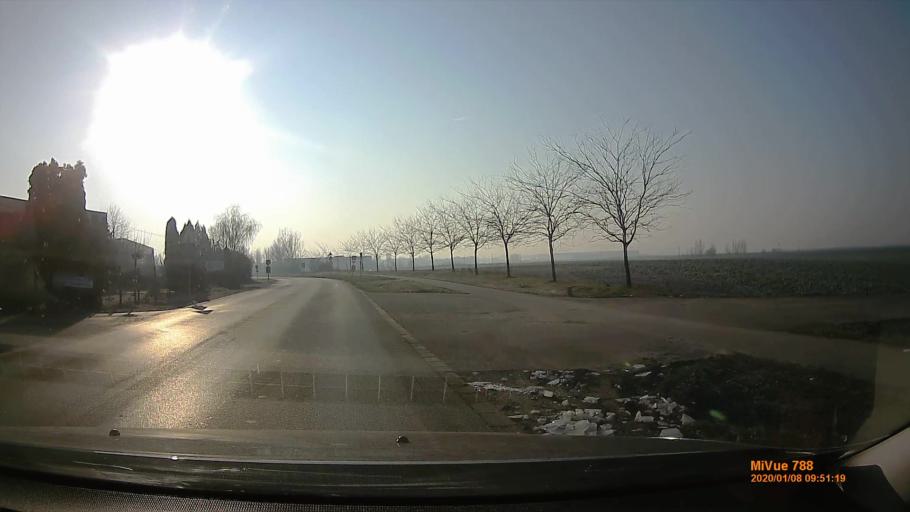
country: HU
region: Bacs-Kiskun
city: Kecskemet
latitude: 46.8755
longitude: 19.6995
